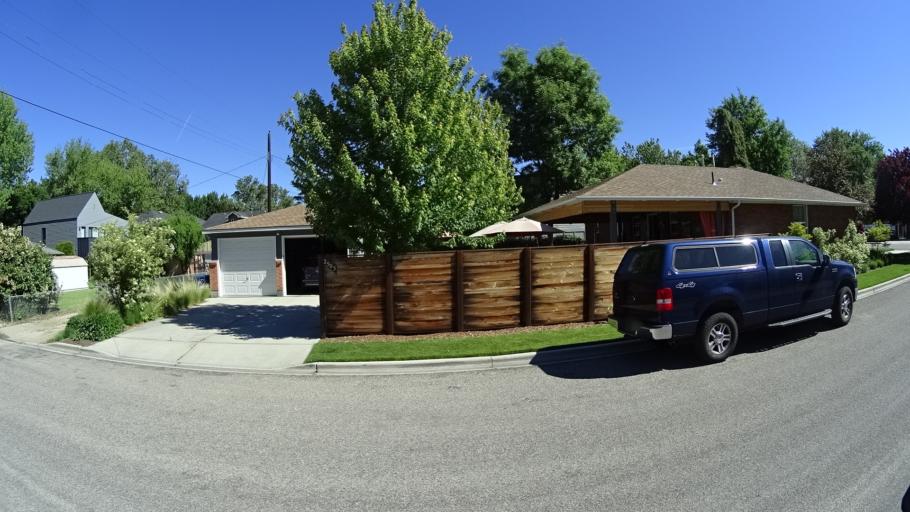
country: US
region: Idaho
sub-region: Ada County
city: Garden City
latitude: 43.6426
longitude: -116.2251
